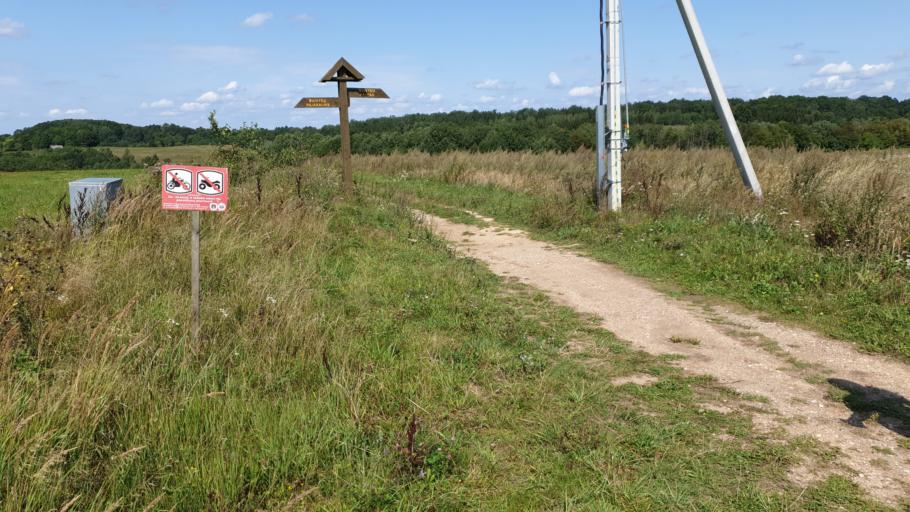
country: LT
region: Vilnius County
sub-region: Vilniaus Rajonas
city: Vievis
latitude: 54.8212
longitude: 24.9459
